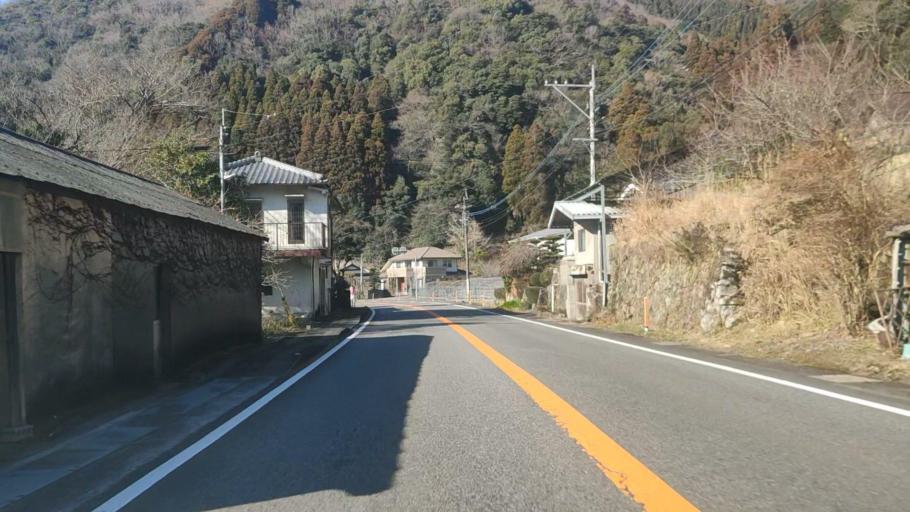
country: JP
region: Oita
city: Usuki
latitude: 33.0066
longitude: 131.7411
